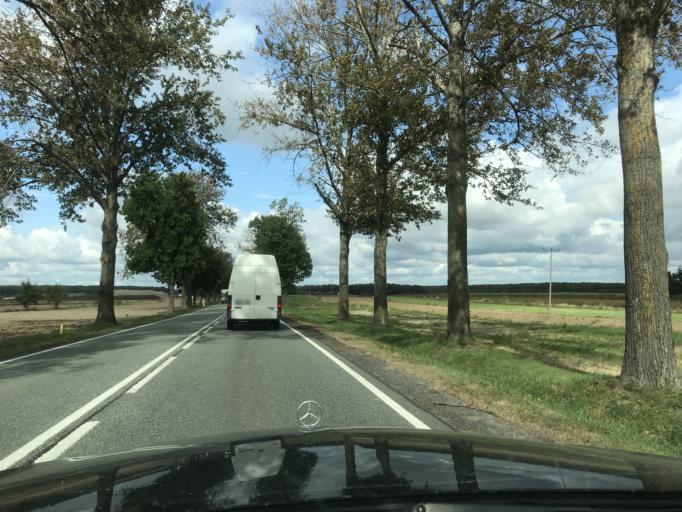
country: PL
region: Lublin Voivodeship
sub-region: Powiat krasnicki
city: Szastarka
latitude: 50.8334
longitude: 22.3054
